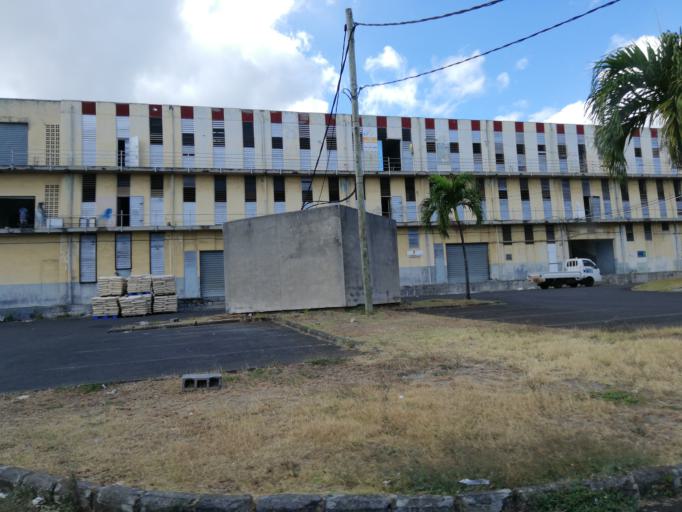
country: MU
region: Black River
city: Petite Riviere
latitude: -20.1897
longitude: 57.4666
